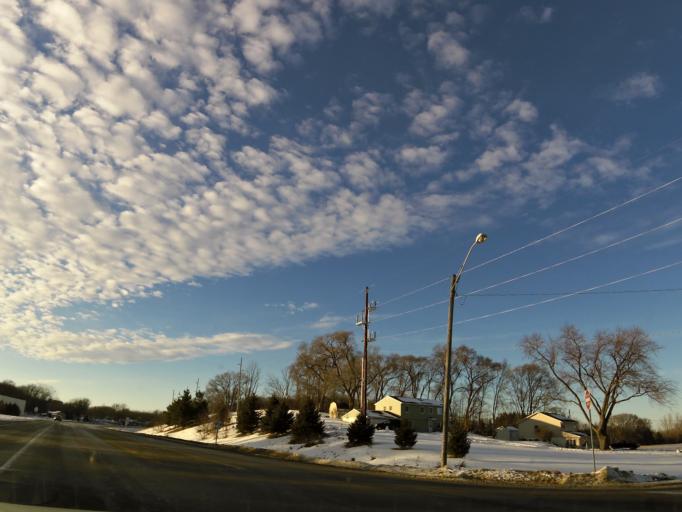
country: US
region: Iowa
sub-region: Butler County
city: Shell Rock
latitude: 42.7158
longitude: -92.5746
